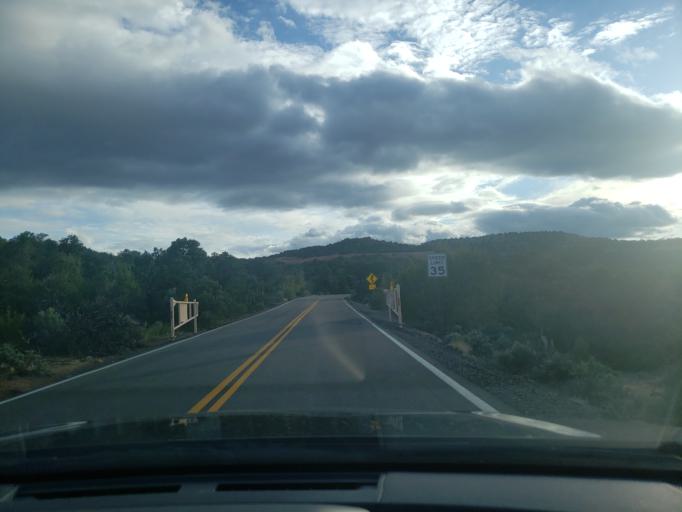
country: US
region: Colorado
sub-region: Mesa County
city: Redlands
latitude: 39.0270
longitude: -108.6586
